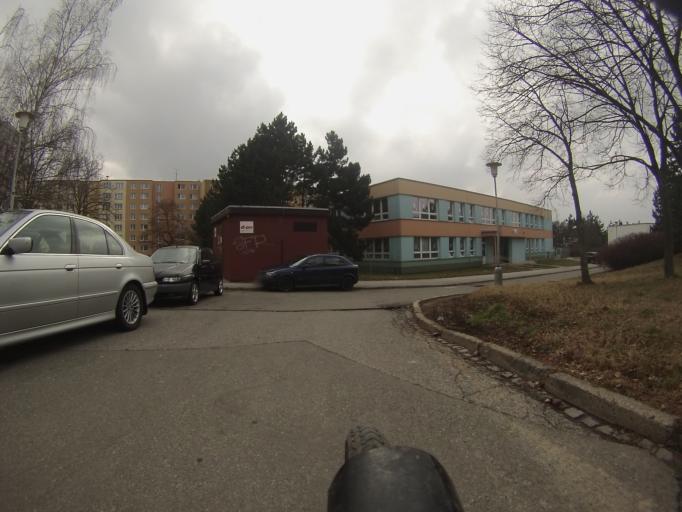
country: CZ
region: South Moravian
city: Bilovice nad Svitavou
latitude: 49.2105
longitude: 16.6780
